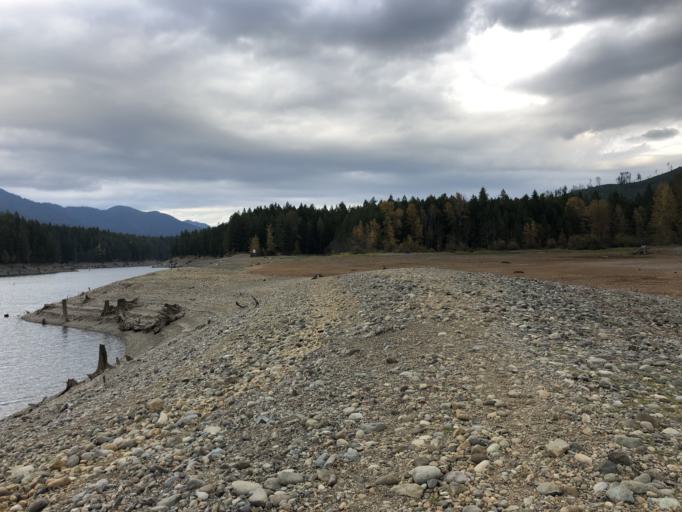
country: US
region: Washington
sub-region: Mason County
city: Shelton
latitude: 47.4625
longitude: -123.2249
